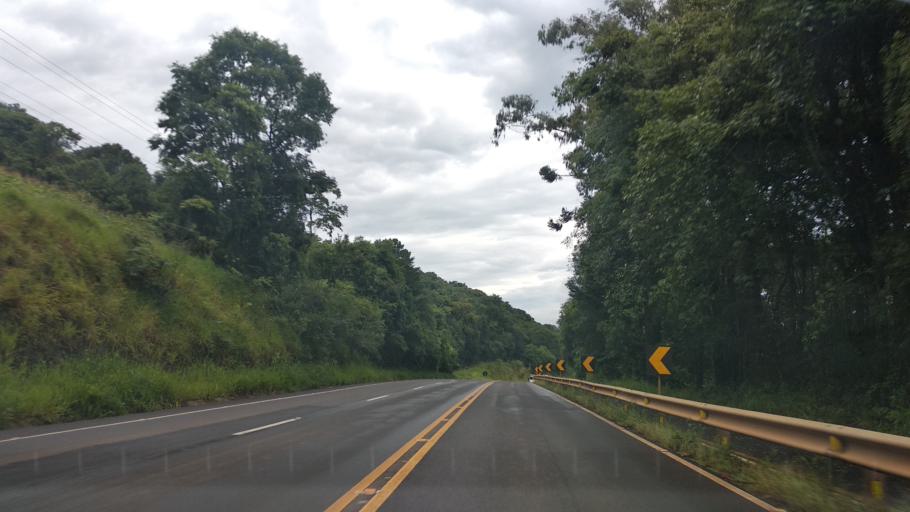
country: BR
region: Santa Catarina
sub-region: Videira
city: Videira
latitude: -27.0876
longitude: -51.2416
